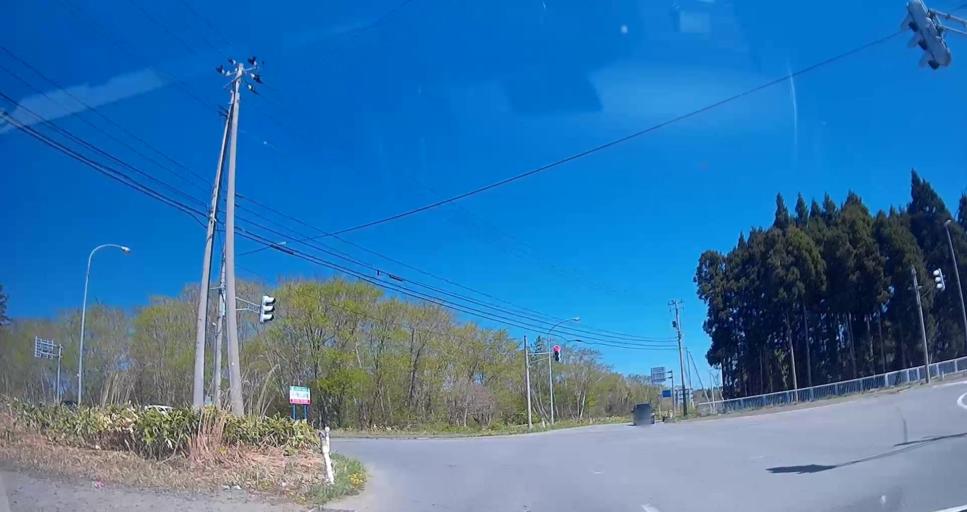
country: JP
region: Aomori
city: Misawa
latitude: 40.9130
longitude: 141.3730
